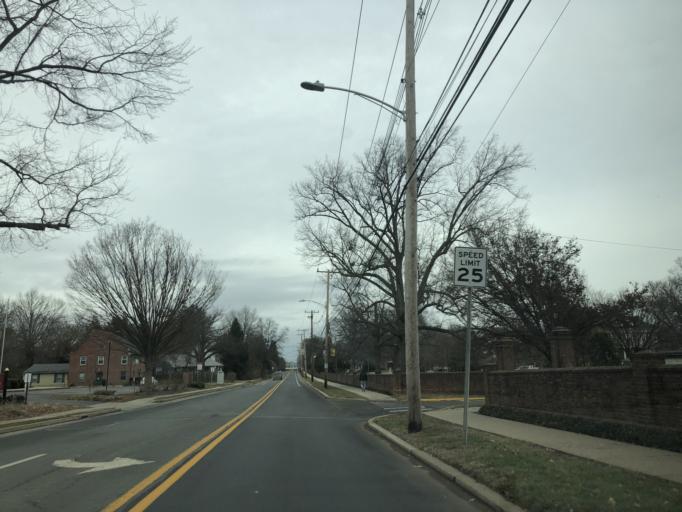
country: US
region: Delaware
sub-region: New Castle County
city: Newark
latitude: 39.6747
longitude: -75.7535
